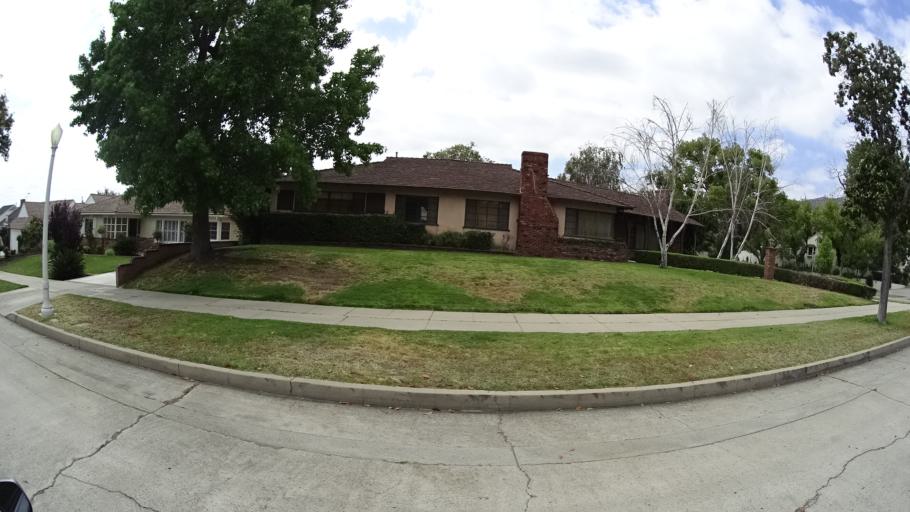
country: US
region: California
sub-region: Los Angeles County
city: Burbank
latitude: 34.1962
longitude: -118.3188
